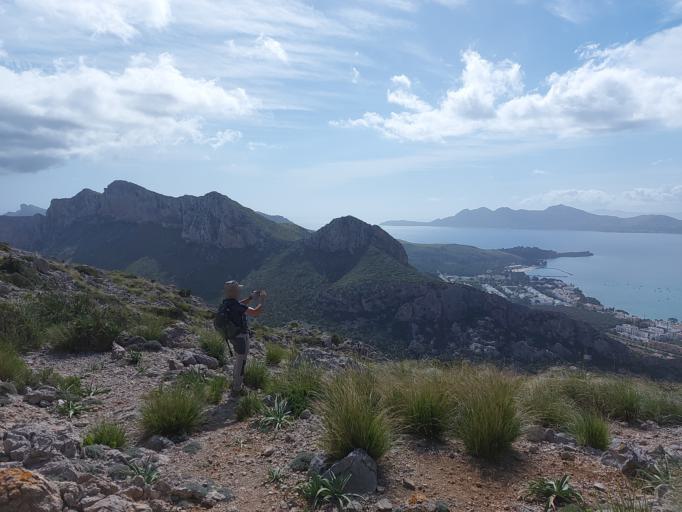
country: ES
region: Balearic Islands
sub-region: Illes Balears
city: Pollenca
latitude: 39.9205
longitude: 3.0770
